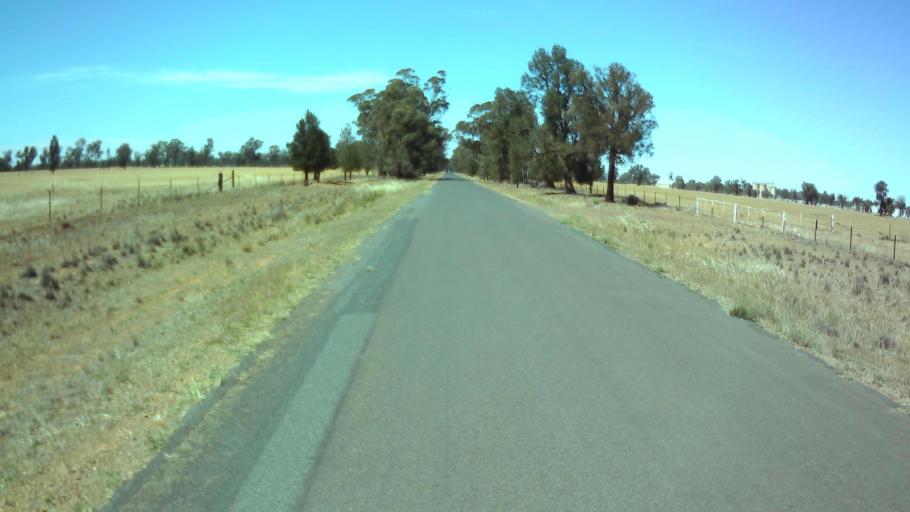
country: AU
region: New South Wales
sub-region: Weddin
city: Grenfell
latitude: -34.1077
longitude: 147.8863
